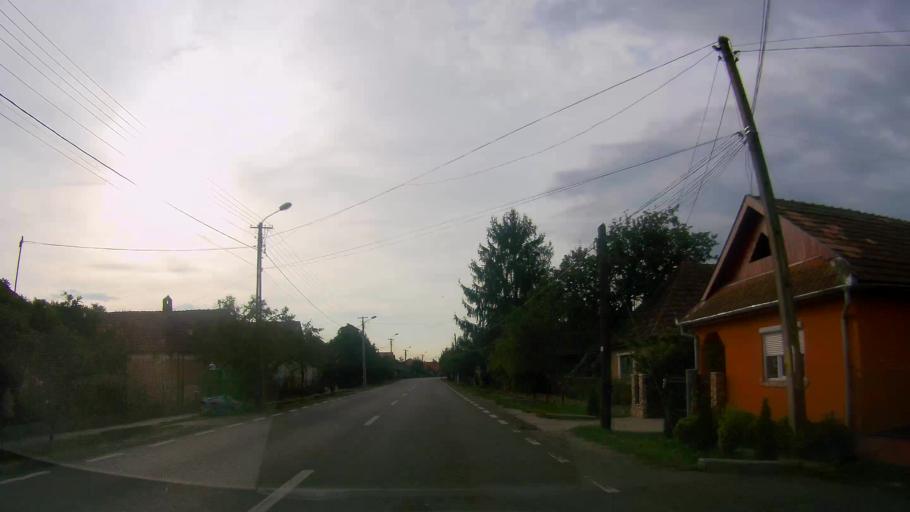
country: RO
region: Satu Mare
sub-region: Comuna Turulung
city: Turulung
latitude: 47.9465
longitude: 23.0727
